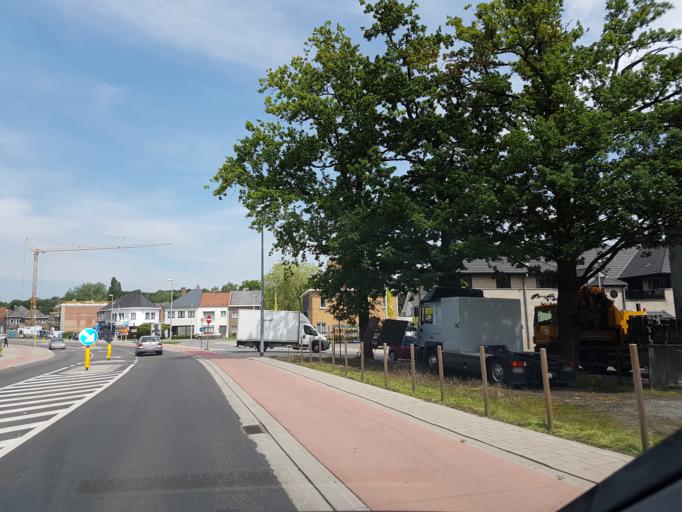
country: BE
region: Flanders
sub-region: Provincie Oost-Vlaanderen
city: Aalst
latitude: 50.9271
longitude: 4.0677
